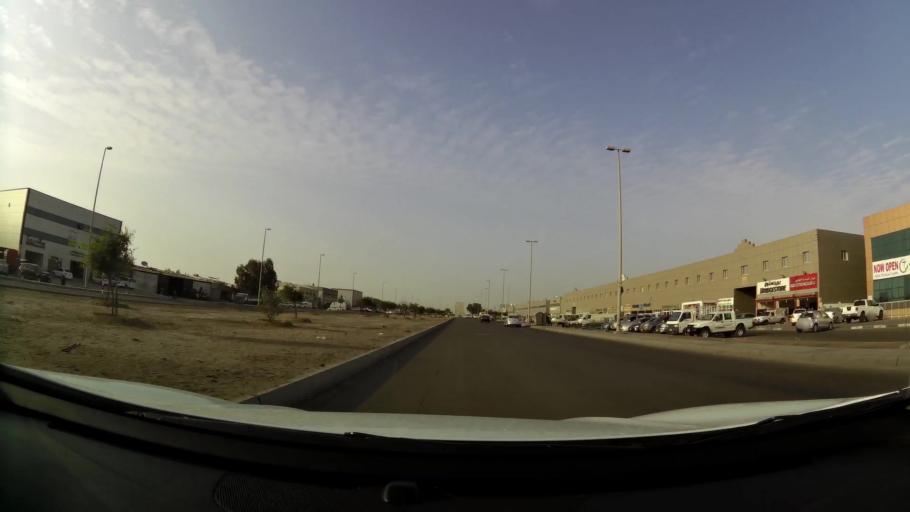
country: AE
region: Abu Dhabi
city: Abu Dhabi
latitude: 24.3698
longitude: 54.5163
